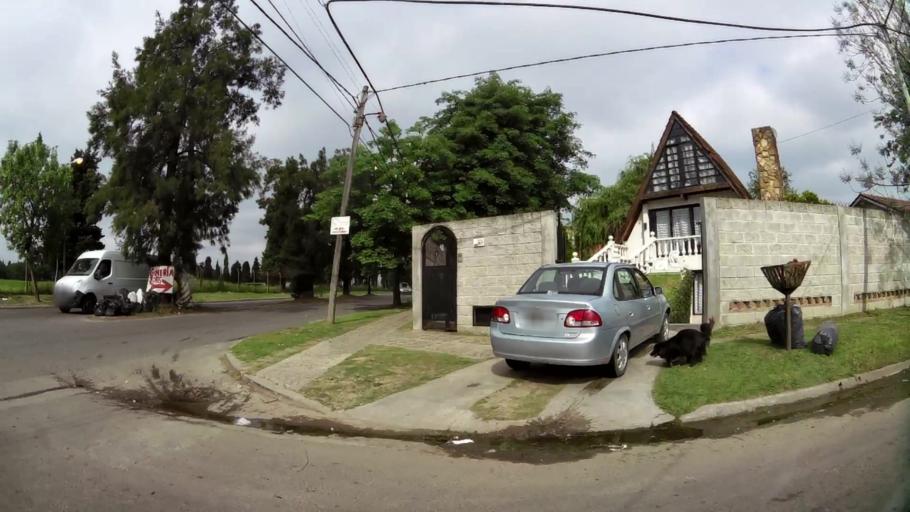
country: AR
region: Buenos Aires
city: San Justo
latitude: -34.7158
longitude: -58.5341
